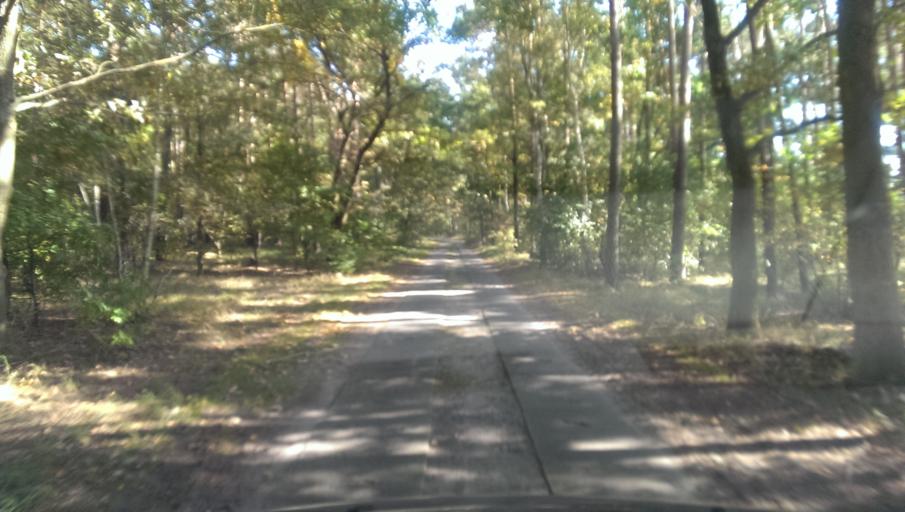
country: DE
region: Brandenburg
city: Sperenberg
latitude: 52.1915
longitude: 13.3357
